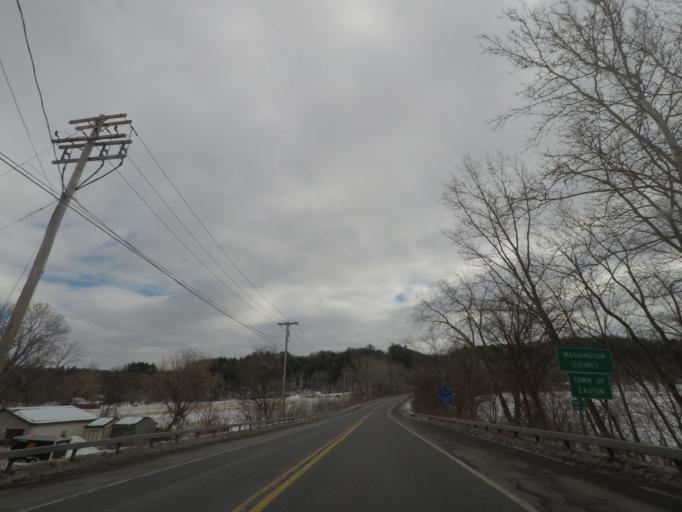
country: US
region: New York
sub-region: Saratoga County
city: Schuylerville
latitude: 43.0977
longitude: -73.5722
